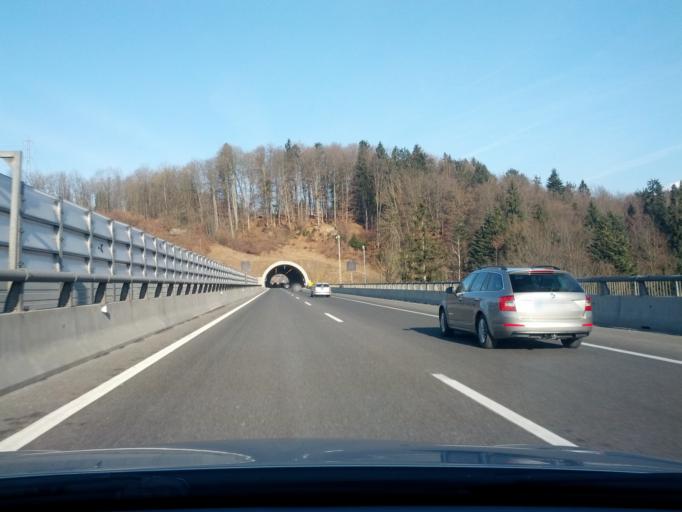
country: SI
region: Trzic
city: Bistrica pri Trzicu
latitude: 46.3165
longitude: 14.2485
